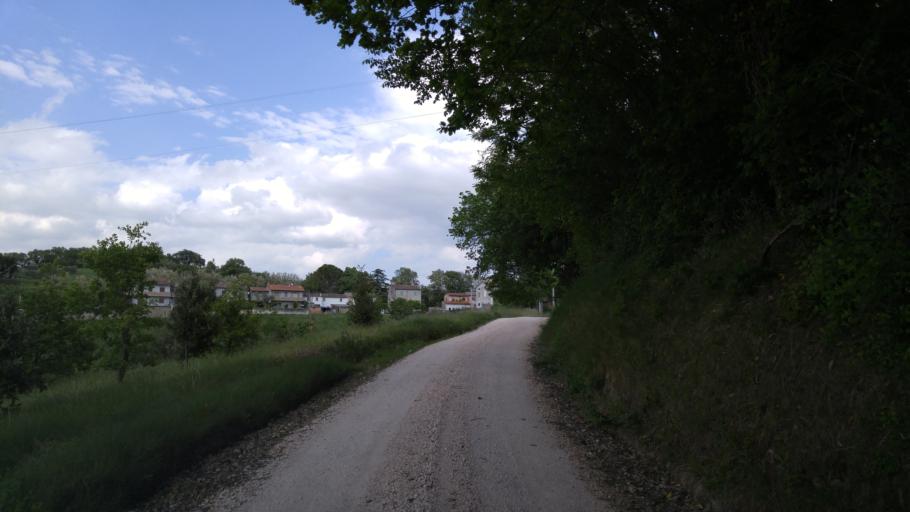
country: IT
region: The Marches
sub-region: Provincia di Pesaro e Urbino
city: Montefelcino
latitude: 43.7272
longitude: 12.8401
